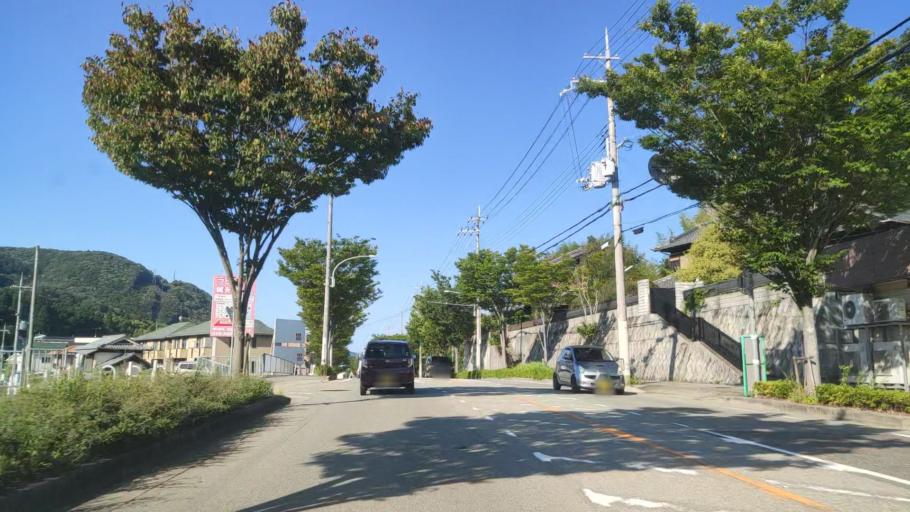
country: JP
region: Hyogo
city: Kobe
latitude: 34.7645
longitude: 135.1780
